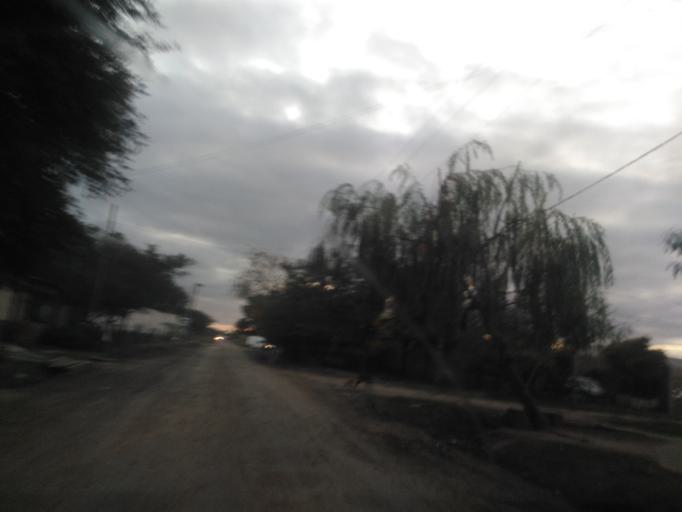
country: AR
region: Chaco
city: Fontana
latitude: -27.4024
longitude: -58.9921
